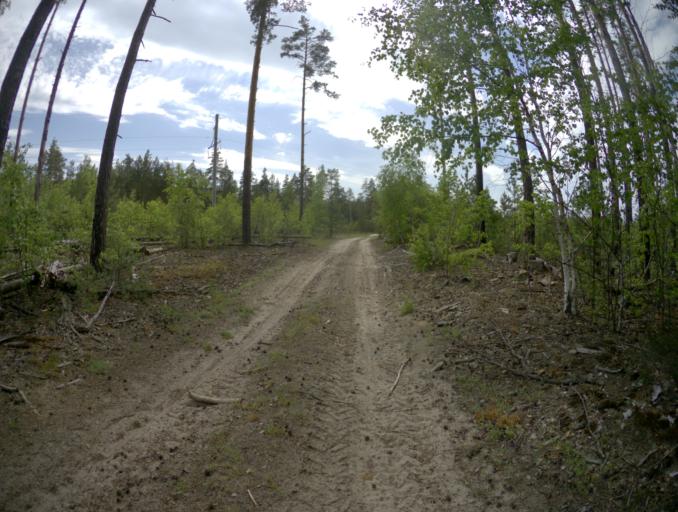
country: RU
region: Vladimir
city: Ivanishchi
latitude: 55.6989
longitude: 40.4328
